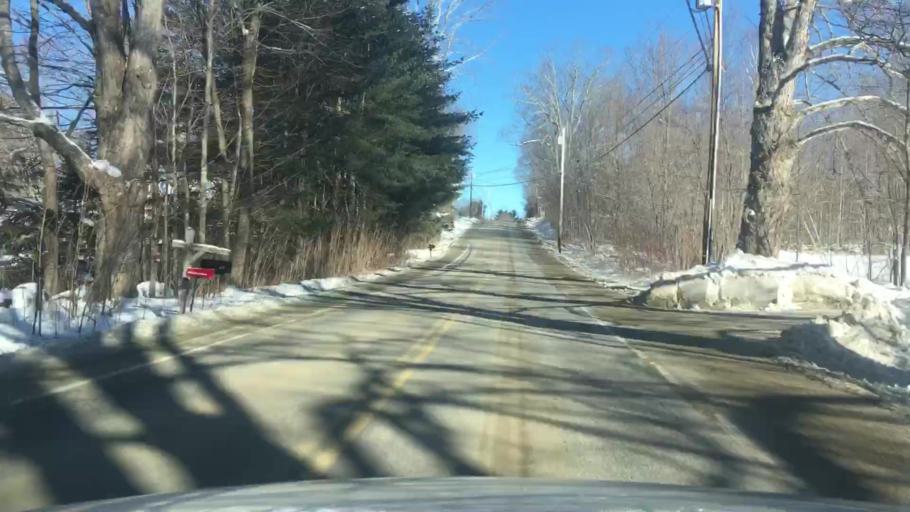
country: US
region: Maine
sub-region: Kennebec County
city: Readfield
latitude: 44.3960
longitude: -69.9642
